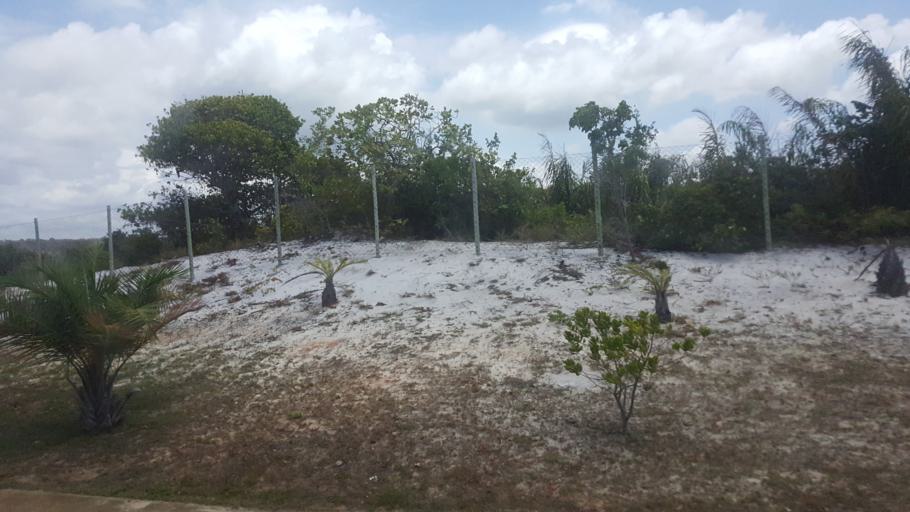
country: BR
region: Bahia
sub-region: Mata De Sao Joao
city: Mata de Sao Joao
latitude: -12.4821
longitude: -37.9601
